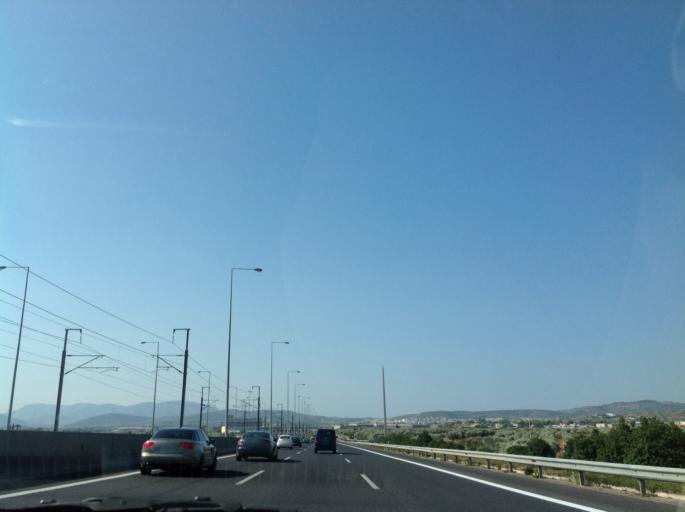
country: GR
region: Attica
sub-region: Nomarchia Anatolikis Attikis
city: Karellas
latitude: 37.9465
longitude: 23.8861
